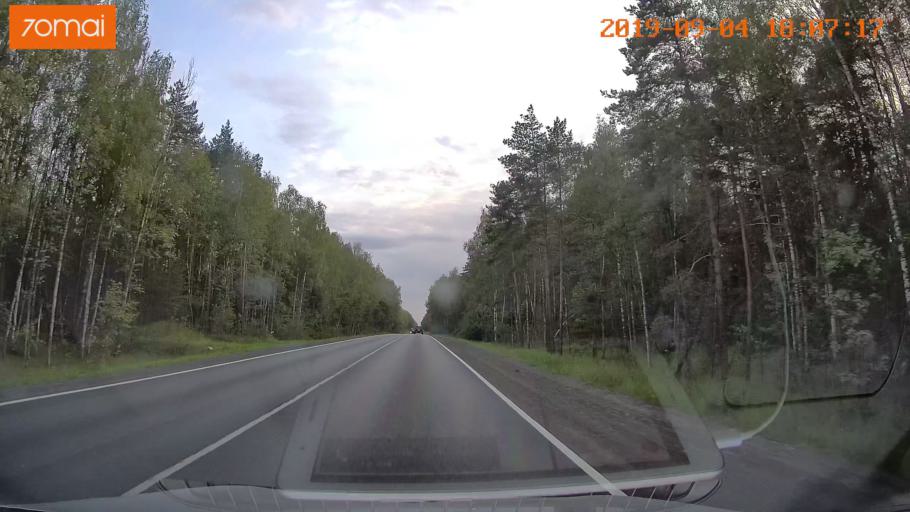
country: RU
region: Moskovskaya
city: Khorlovo
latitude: 55.4210
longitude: 38.8031
